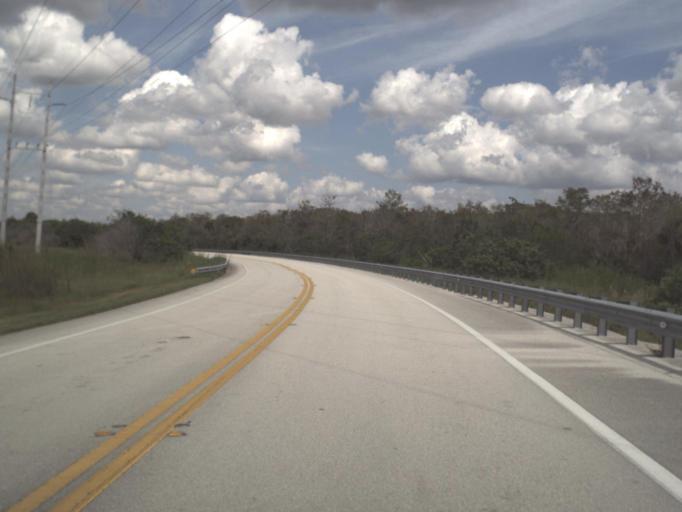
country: US
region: Florida
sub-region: Collier County
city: Marco
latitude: 25.9201
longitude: -81.3587
